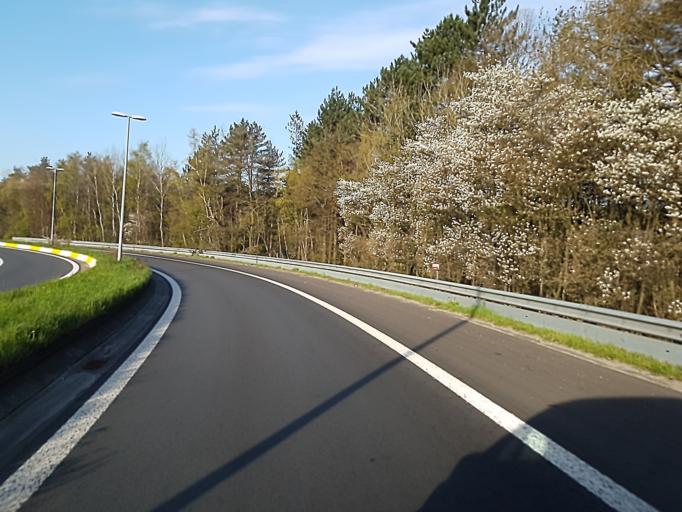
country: BE
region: Flanders
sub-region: Provincie Antwerpen
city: Vosselaar
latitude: 51.2991
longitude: 4.9100
